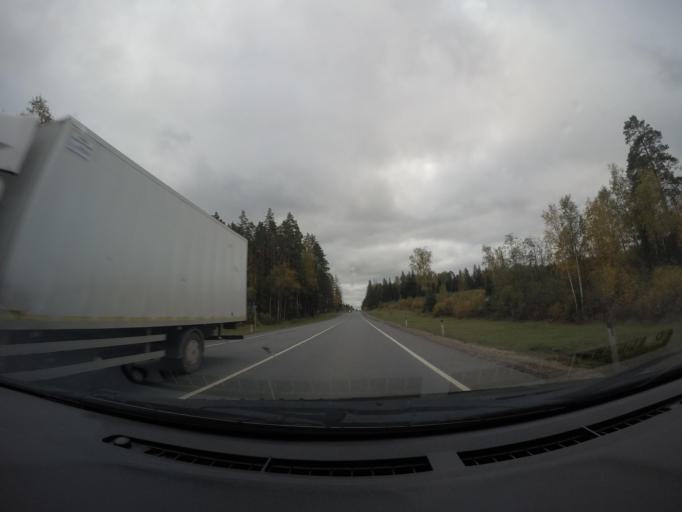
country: RU
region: Moskovskaya
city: Dorokhovo
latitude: 55.6147
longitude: 36.3486
